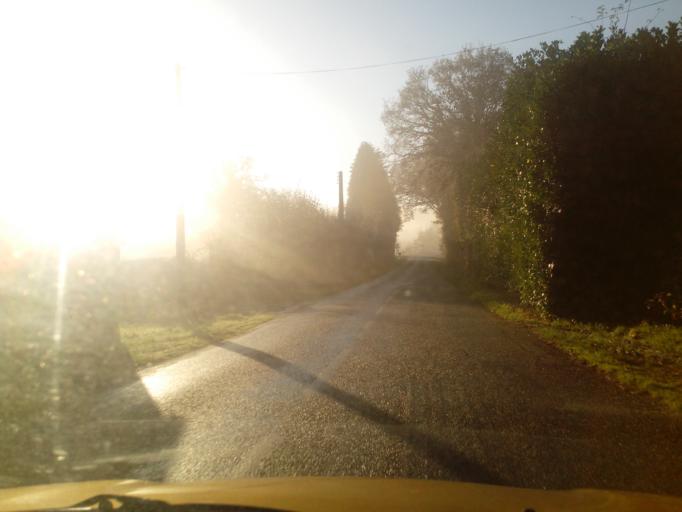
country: FR
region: Brittany
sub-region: Departement du Morbihan
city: Pluherlin
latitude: 47.7129
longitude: -2.3376
